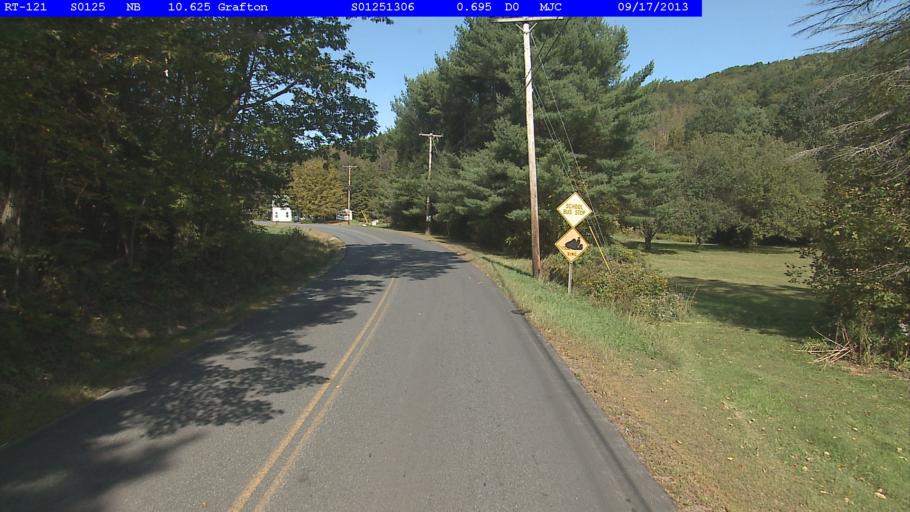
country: US
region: Vermont
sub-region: Windham County
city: Rockingham
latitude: 43.1560
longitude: -72.5659
